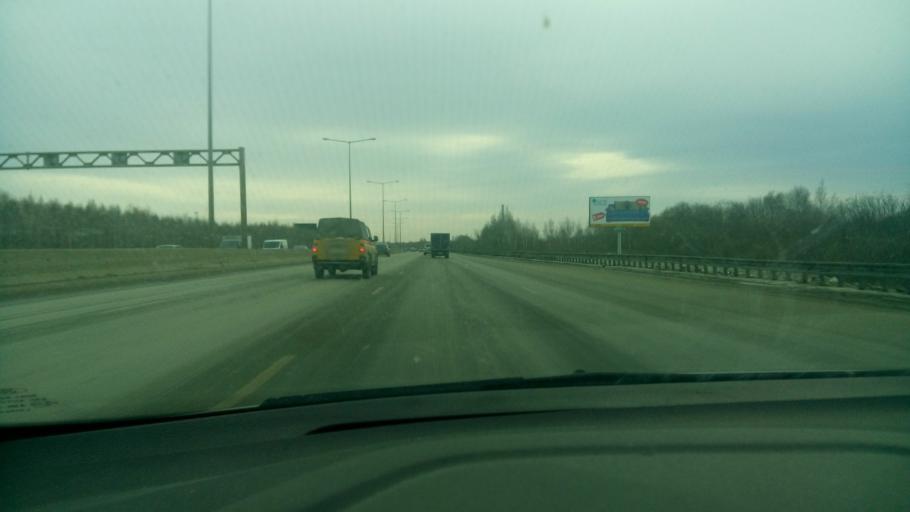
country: RU
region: Sverdlovsk
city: Istok
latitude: 56.7660
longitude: 60.7429
